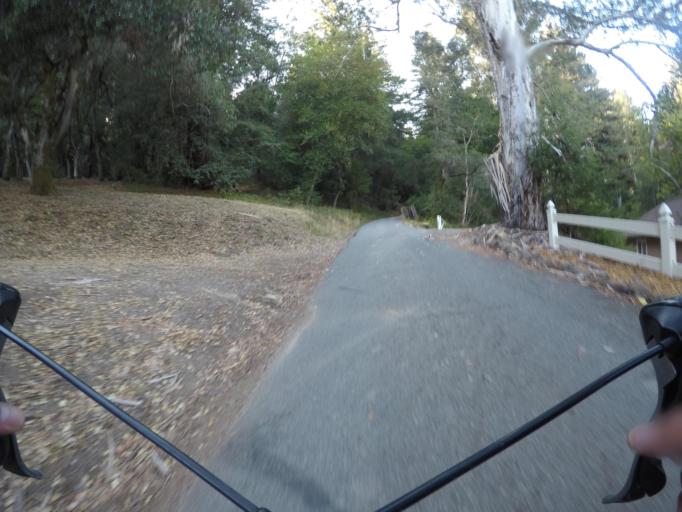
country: US
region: California
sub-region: Santa Cruz County
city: Brookdale
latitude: 37.1079
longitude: -122.0953
